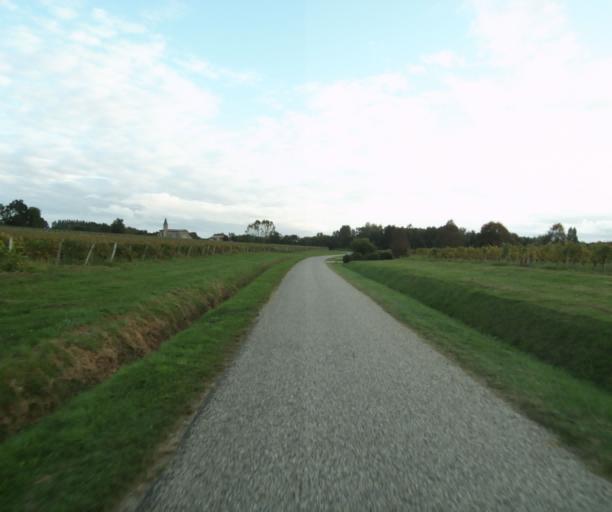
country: FR
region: Aquitaine
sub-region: Departement des Landes
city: Gabarret
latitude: 43.9671
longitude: 0.0825
